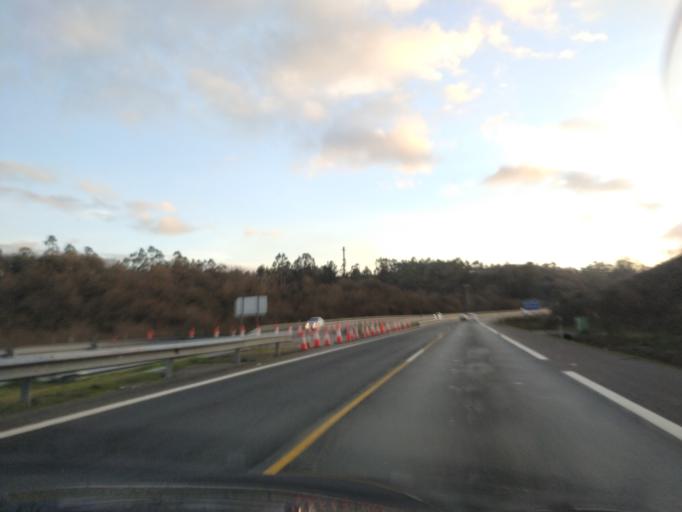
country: ES
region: Galicia
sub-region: Provincia da Coruna
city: Santiago de Compostela
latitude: 42.9011
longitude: -8.4676
